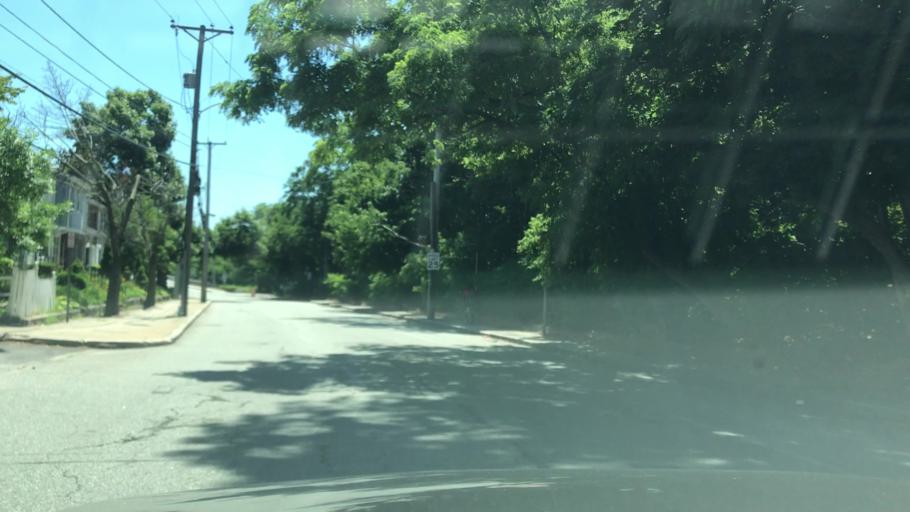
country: US
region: Rhode Island
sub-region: Providence County
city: Pawtucket
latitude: 41.8708
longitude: -71.3801
